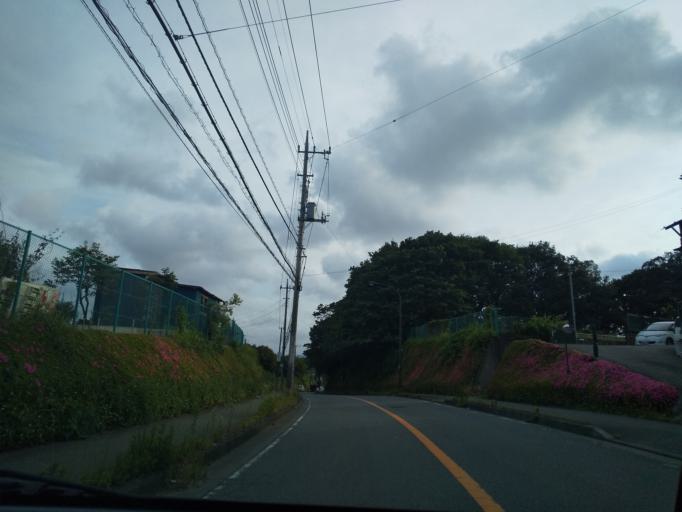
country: JP
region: Kanagawa
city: Zama
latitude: 35.5140
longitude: 139.3894
